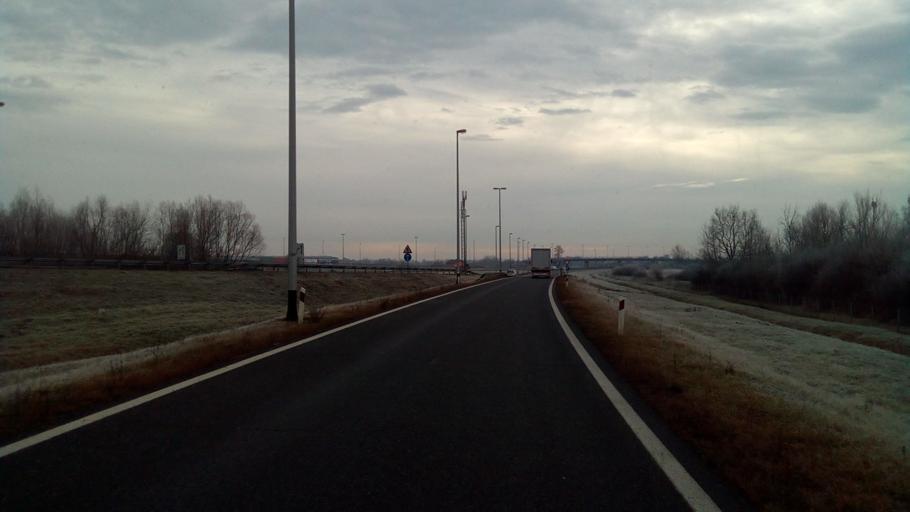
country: HR
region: Grad Zagreb
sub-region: Sesvete
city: Sesvete
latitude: 45.7976
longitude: 16.1293
